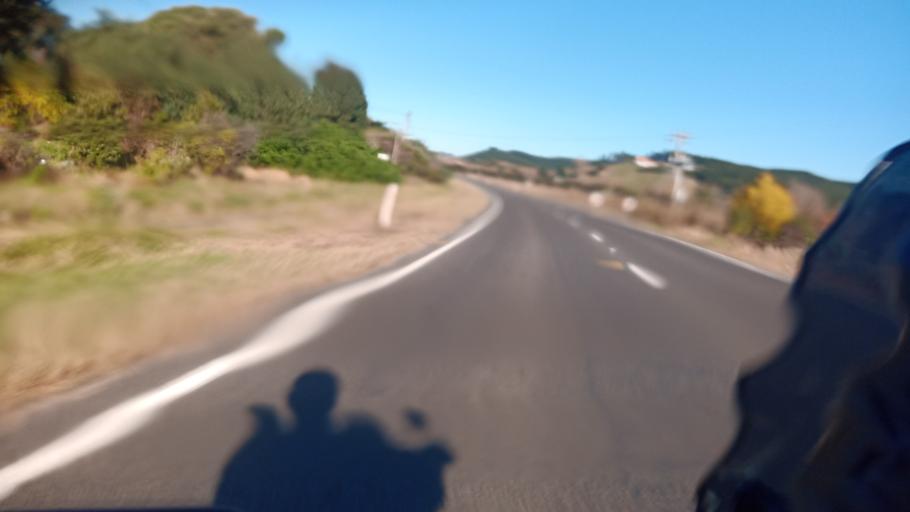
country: NZ
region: Hawke's Bay
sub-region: Napier City
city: Napier
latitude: -39.3655
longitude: 176.9000
